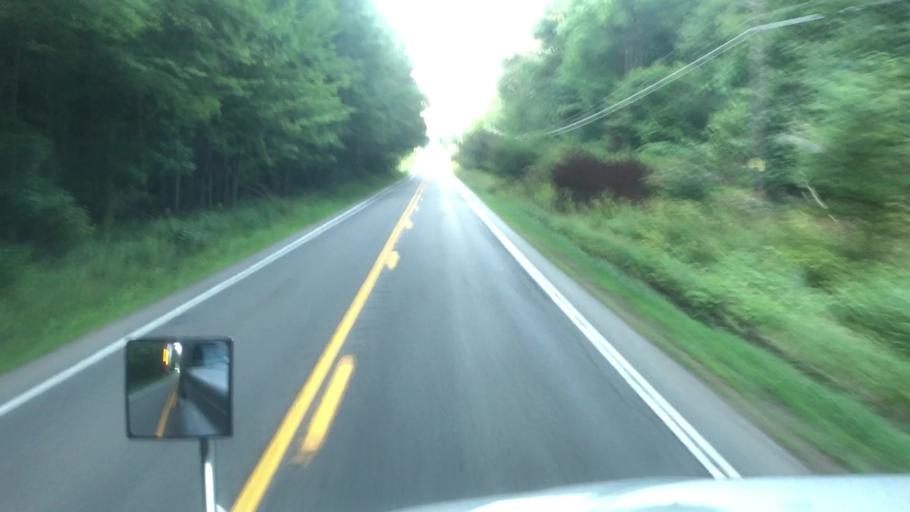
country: US
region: Pennsylvania
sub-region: Crawford County
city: Titusville
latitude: 41.5619
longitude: -79.6111
